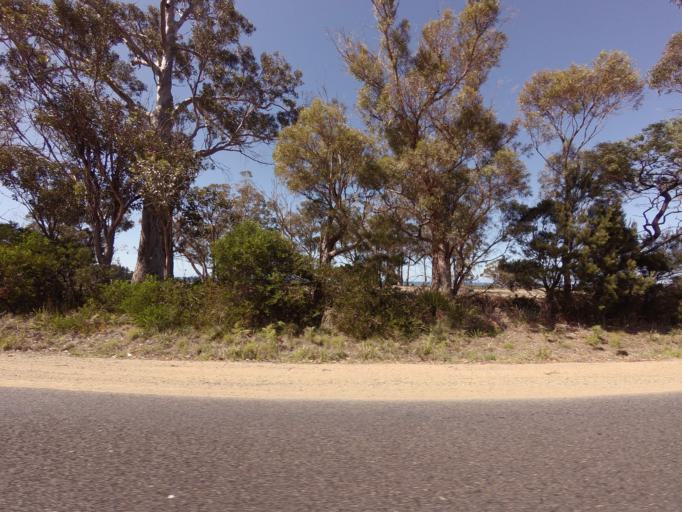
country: AU
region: Tasmania
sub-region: Break O'Day
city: St Helens
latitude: -41.7006
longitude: 148.2756
